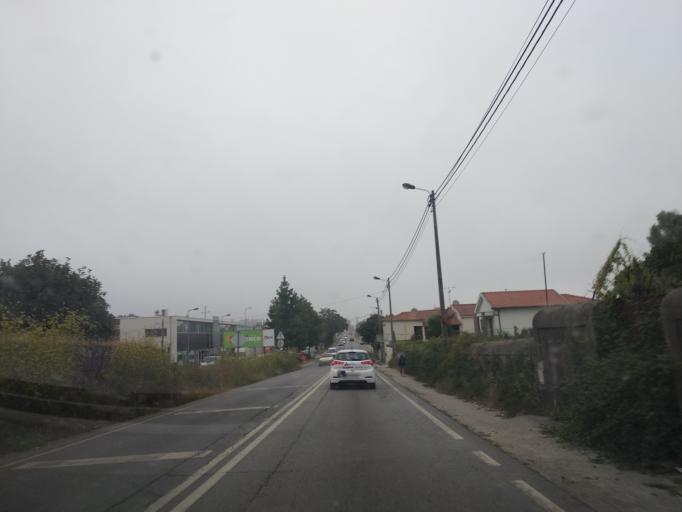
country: PT
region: Braga
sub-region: Vila Verde
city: Vila Verde
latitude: 41.6281
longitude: -8.4334
